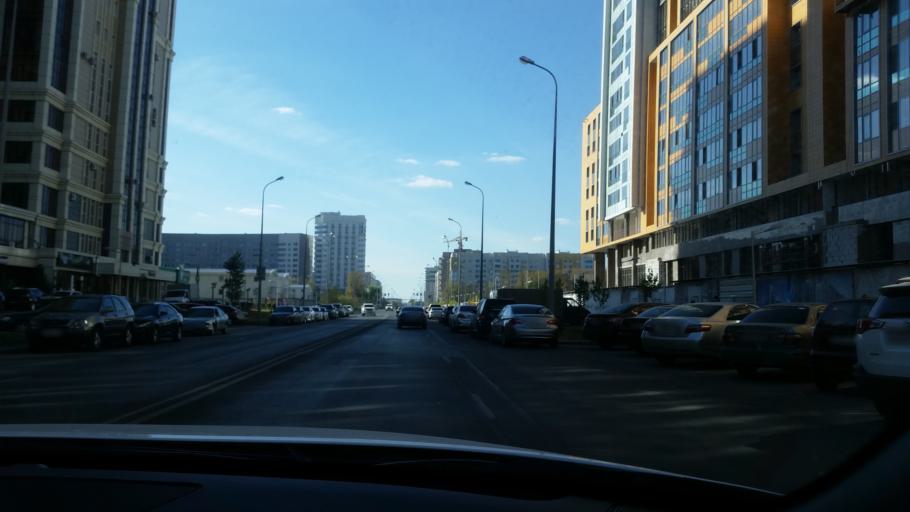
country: KZ
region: Astana Qalasy
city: Astana
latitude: 51.1159
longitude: 71.4296
